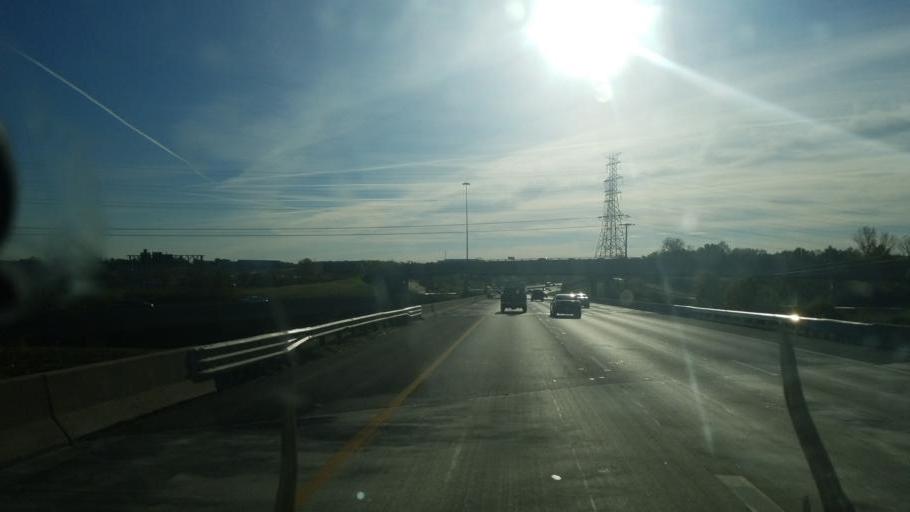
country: US
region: Missouri
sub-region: Saint Louis County
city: Saint Johns
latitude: 38.7288
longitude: -90.3325
